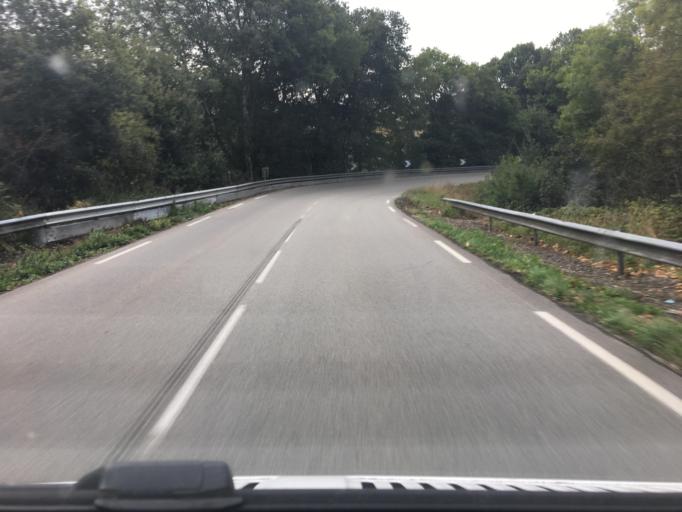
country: FR
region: Brittany
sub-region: Departement du Finistere
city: Chateaulin
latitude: 48.2030
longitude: -4.0799
